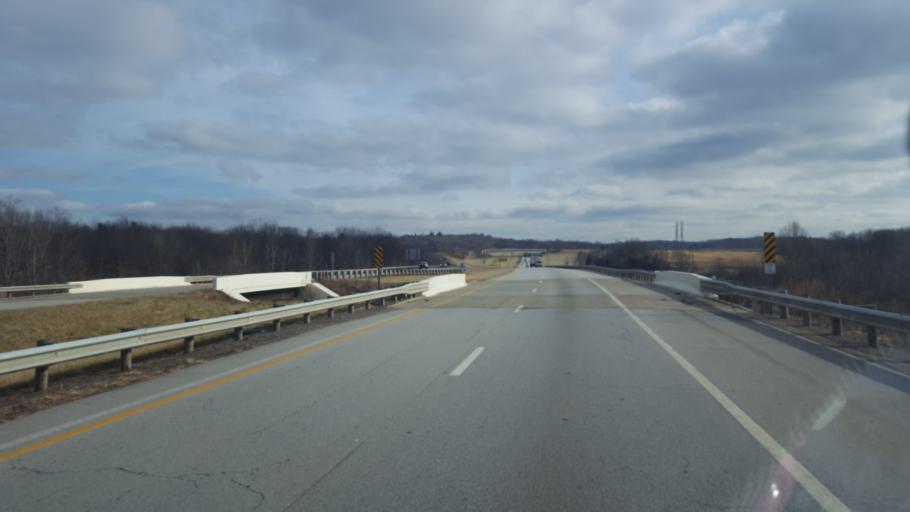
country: US
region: Ohio
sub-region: Stark County
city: East Canton
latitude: 40.7838
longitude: -81.3305
